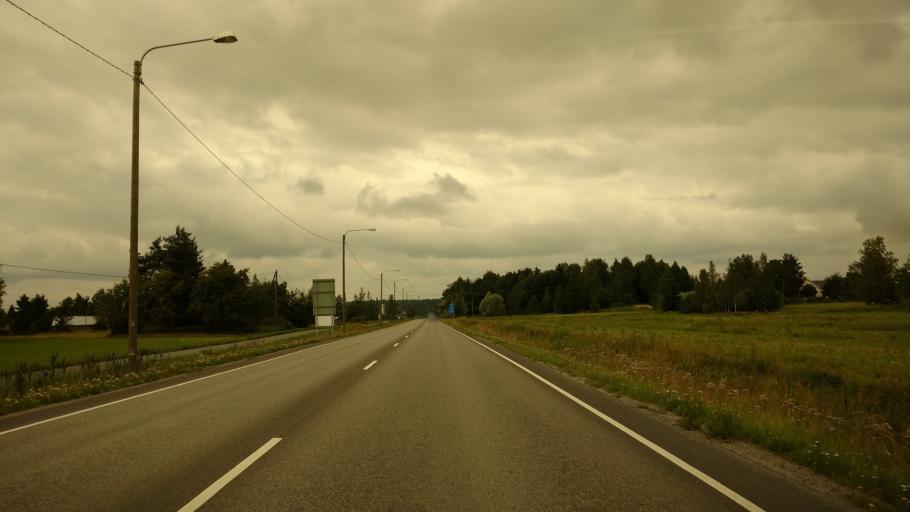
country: FI
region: Varsinais-Suomi
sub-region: Salo
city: Halikko
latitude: 60.4191
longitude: 23.0499
